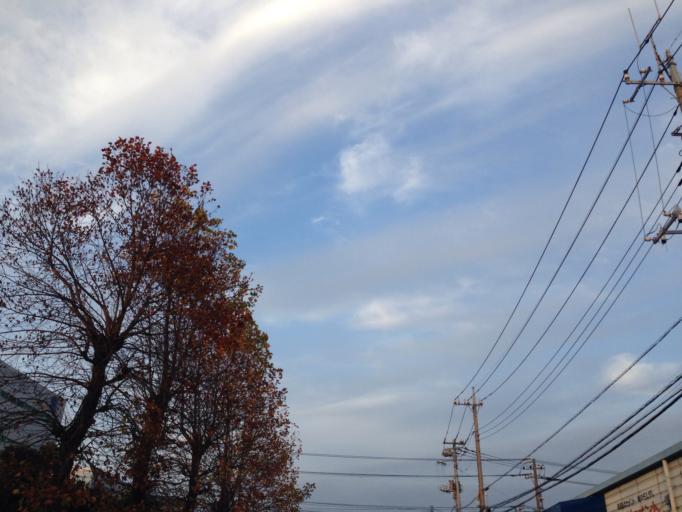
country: JP
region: Chiba
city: Kashiwa
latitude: 35.9052
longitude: 139.9448
